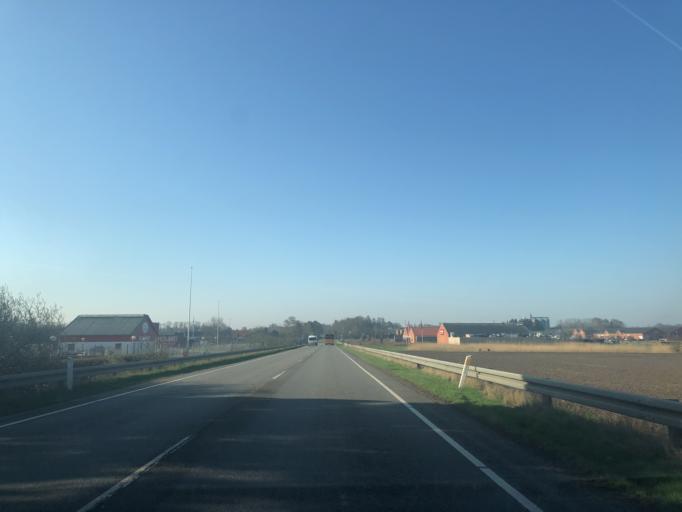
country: DK
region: Zealand
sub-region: Faxe Kommune
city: Haslev
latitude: 55.3333
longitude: 11.9426
